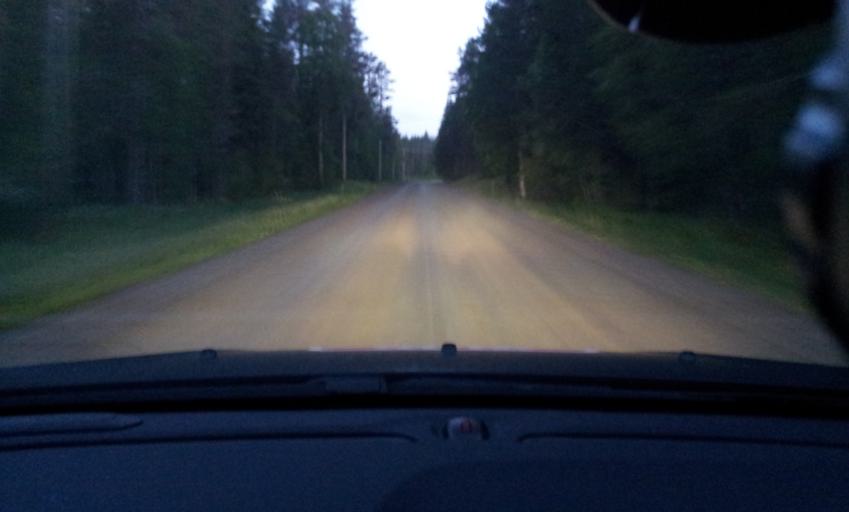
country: SE
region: Jaemtland
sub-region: Braecke Kommun
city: Braecke
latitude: 62.7264
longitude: 15.5220
